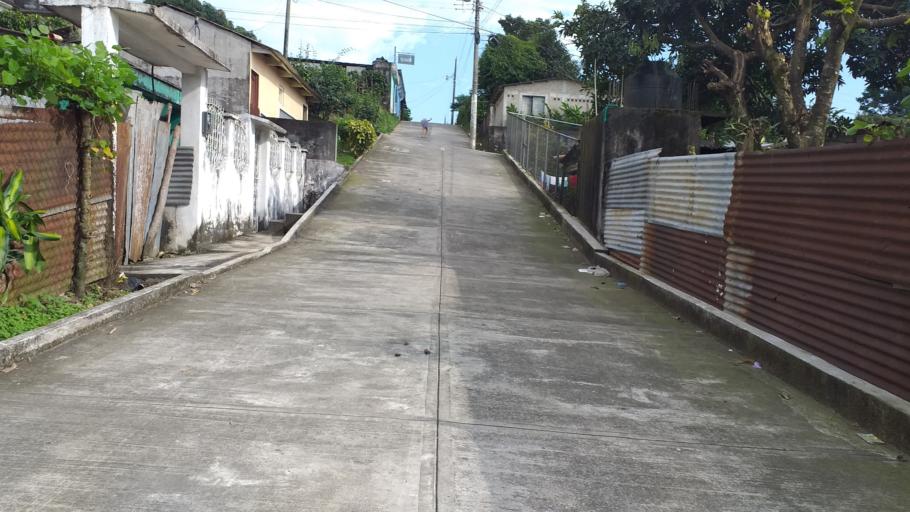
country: GT
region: Suchitepeque
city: Pueblo Nuevo
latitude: 14.6437
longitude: -91.5578
